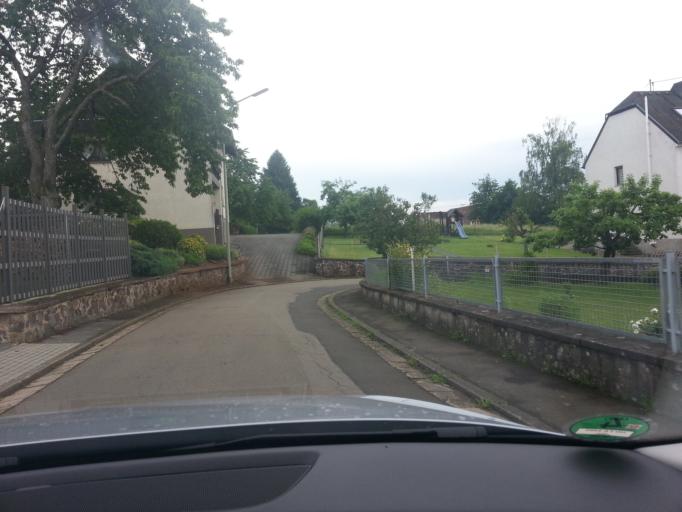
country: DE
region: Saarland
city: Sankt Wendel
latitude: 49.4939
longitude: 7.1655
